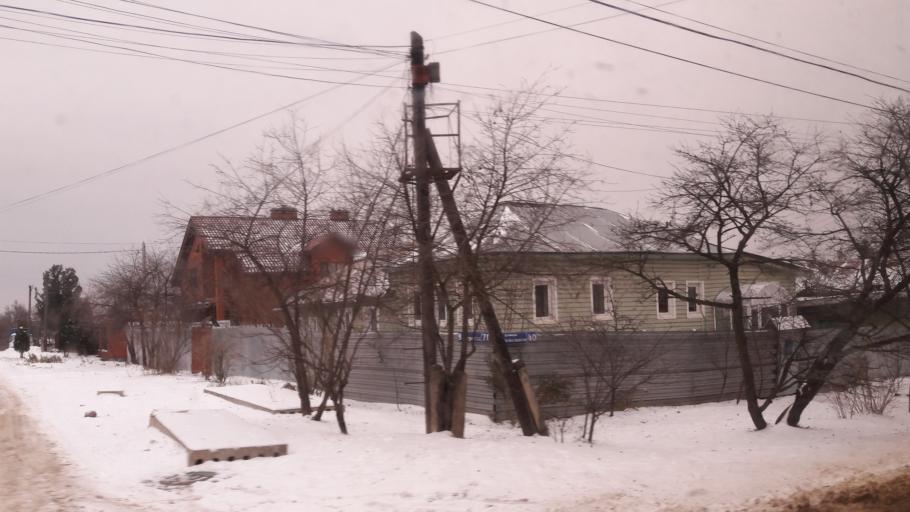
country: RU
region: Tula
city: Gorelki
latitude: 54.2342
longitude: 37.6338
